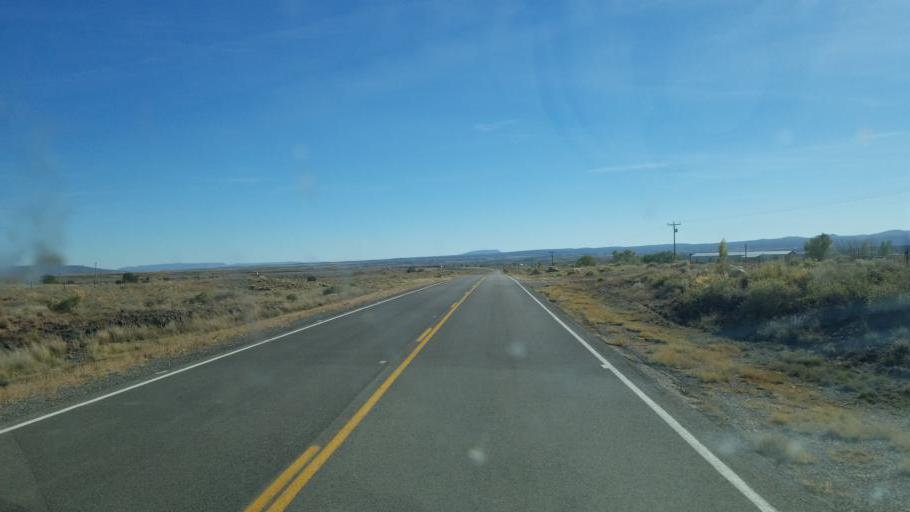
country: US
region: New Mexico
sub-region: Cibola County
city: Milan
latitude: 35.3003
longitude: -107.9874
